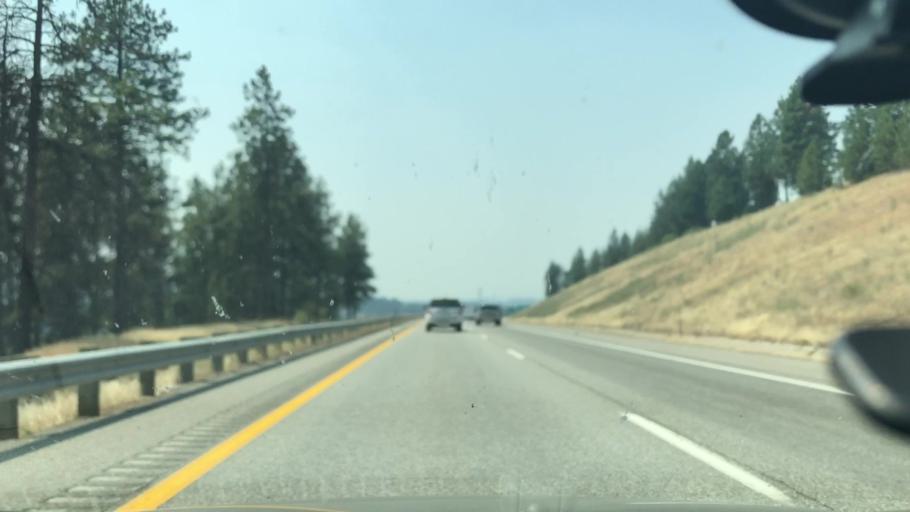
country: US
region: Idaho
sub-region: Kootenai County
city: Post Falls
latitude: 47.7093
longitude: -116.8843
